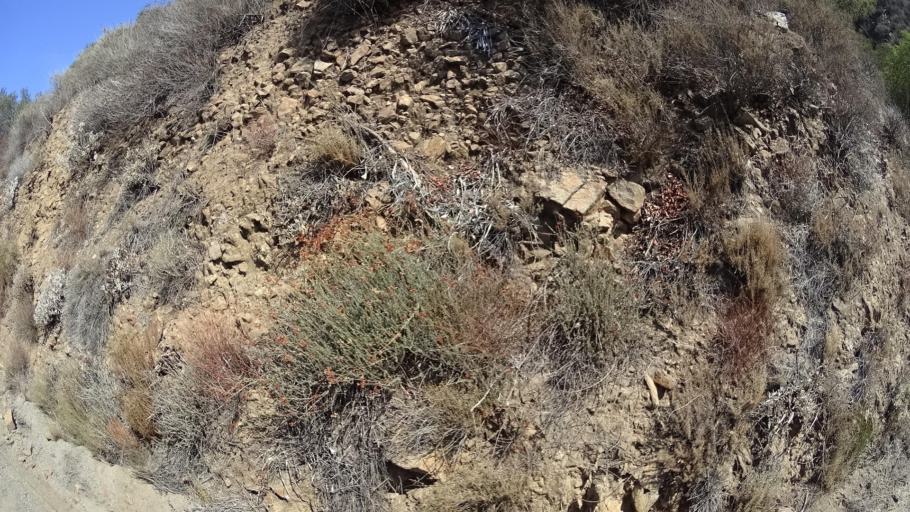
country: US
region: California
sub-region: San Diego County
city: Valley Center
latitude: 33.3325
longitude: -116.9530
